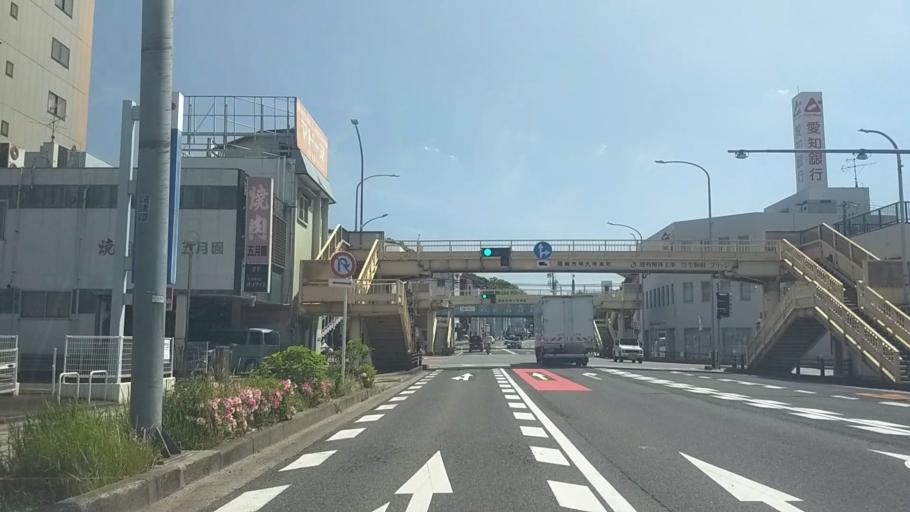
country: JP
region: Aichi
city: Okazaki
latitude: 34.9536
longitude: 137.1641
